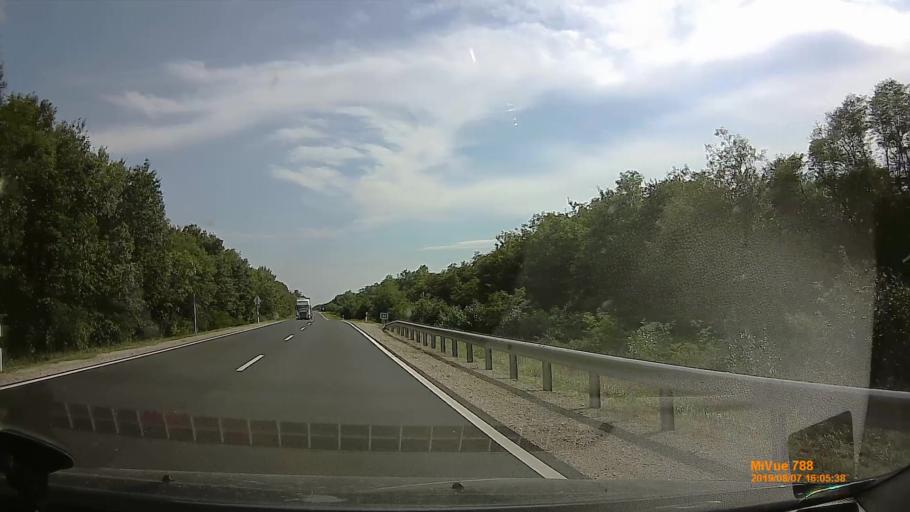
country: HU
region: Vas
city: Kormend
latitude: 46.9515
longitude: 16.6029
